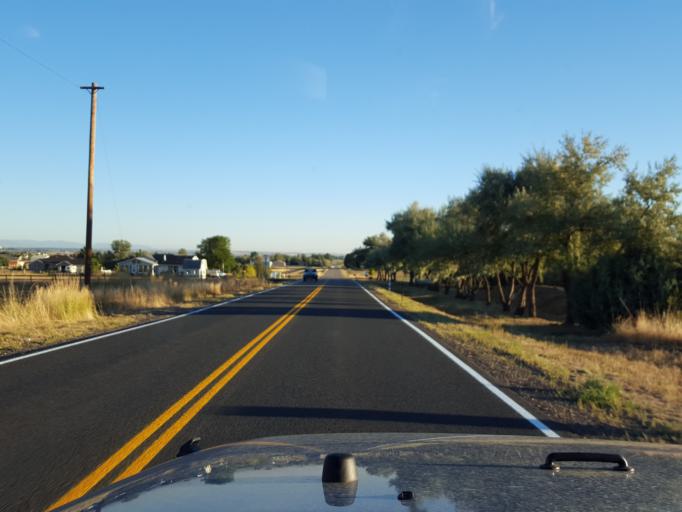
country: US
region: Colorado
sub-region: Boulder County
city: Erie
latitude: 40.0650
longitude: -105.0180
